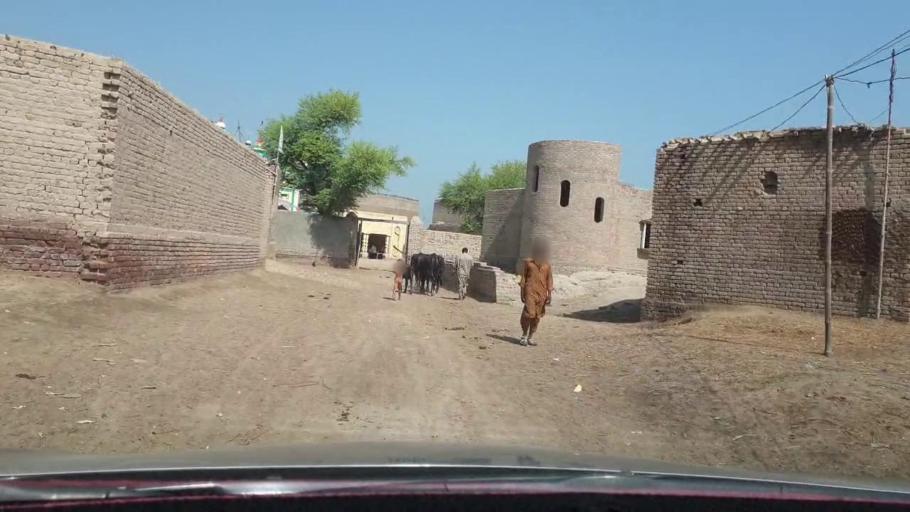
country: PK
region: Sindh
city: Kambar
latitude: 27.5993
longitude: 67.9732
